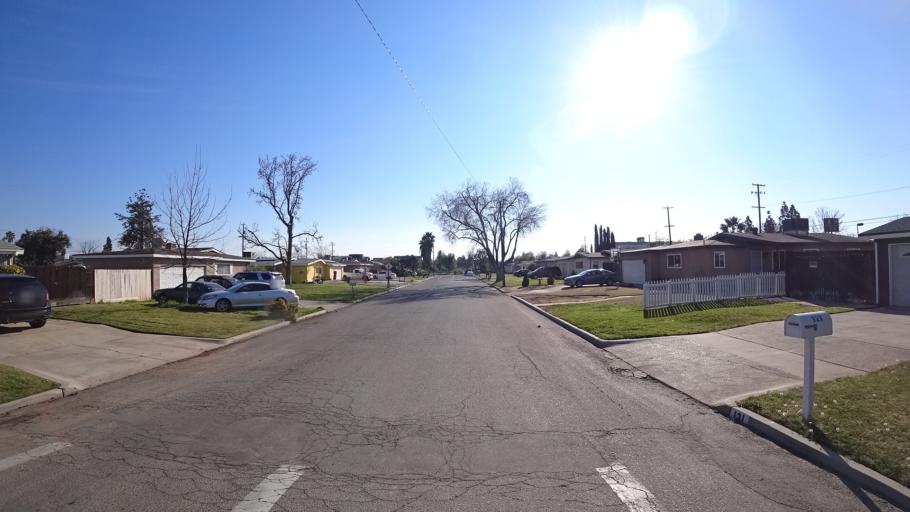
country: US
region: California
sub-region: Fresno County
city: Fresno
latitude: 36.8239
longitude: -119.7877
